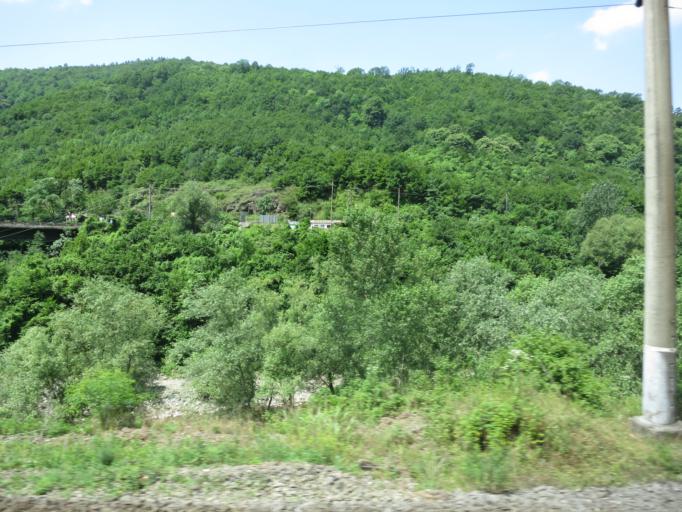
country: GE
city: Shorapani
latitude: 42.0875
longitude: 43.1428
